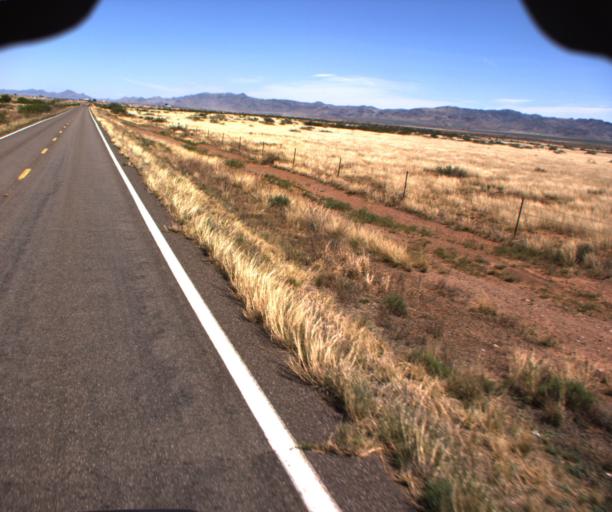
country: US
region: Arizona
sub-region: Cochise County
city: Douglas
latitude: 31.6760
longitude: -109.1429
